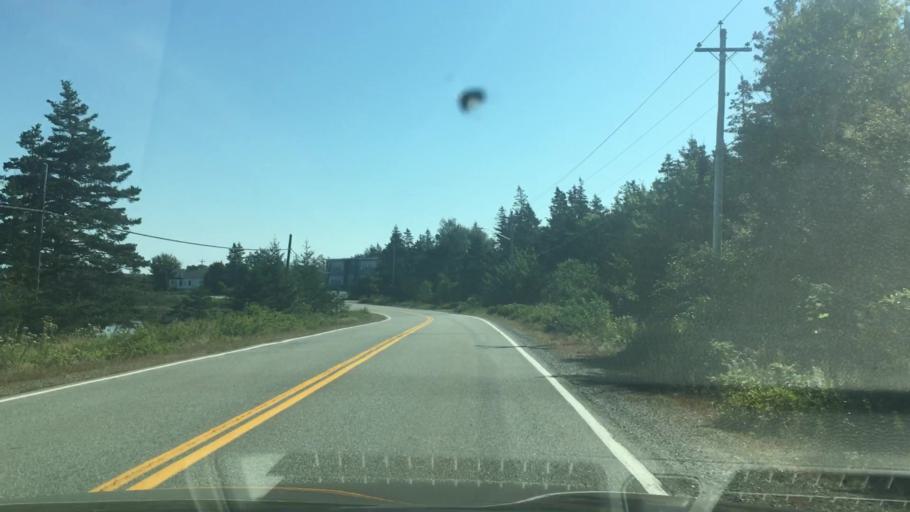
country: CA
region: Nova Scotia
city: New Glasgow
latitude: 44.8034
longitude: -62.6995
